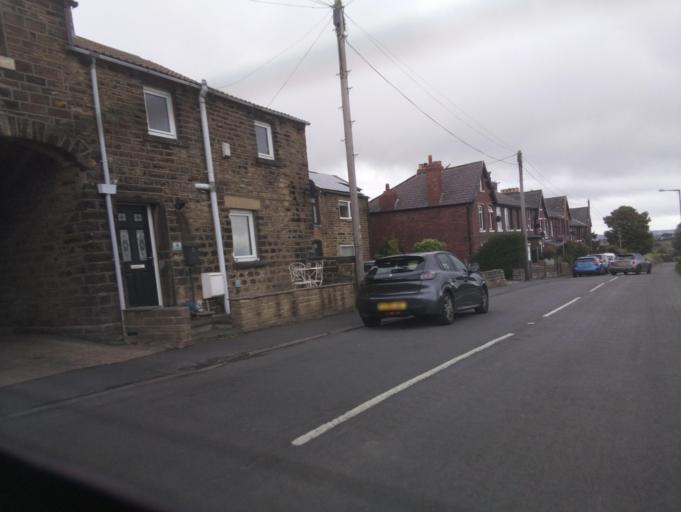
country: GB
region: England
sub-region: Kirklees
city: Shelley
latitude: 53.6142
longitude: -1.6488
